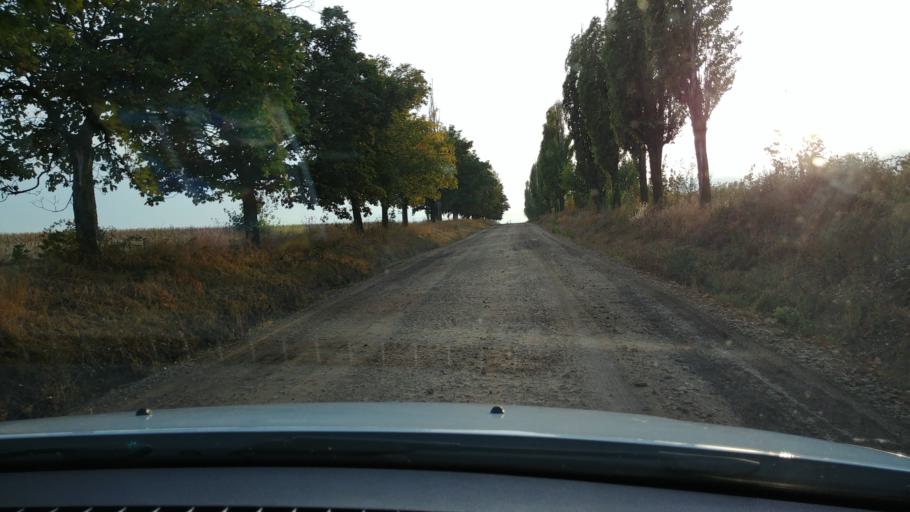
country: MD
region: Rezina
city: Saharna
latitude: 47.6797
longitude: 28.9689
